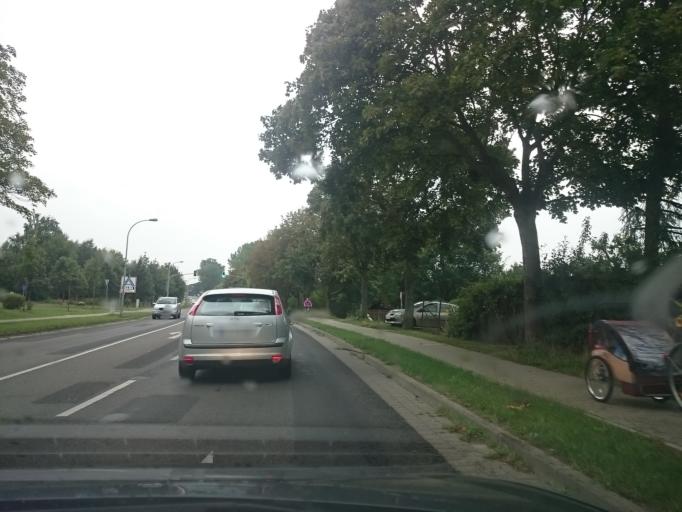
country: DE
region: Brandenburg
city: Gransee
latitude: 53.0034
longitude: 13.1604
